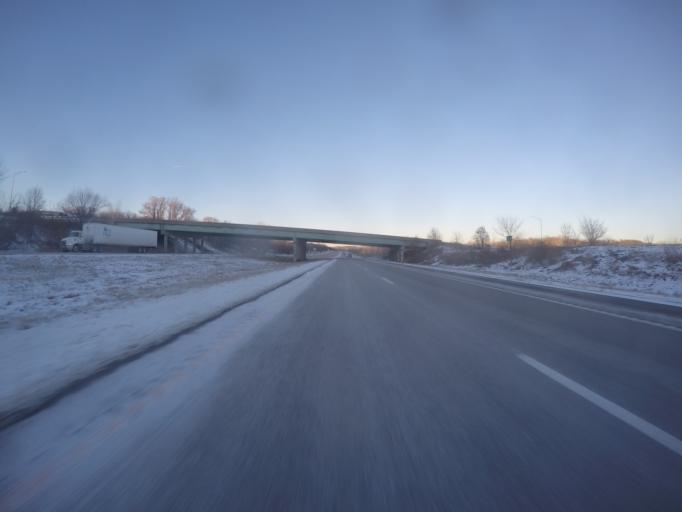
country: US
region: Missouri
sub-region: Platte County
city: Weatherby Lake
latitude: 39.2240
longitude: -94.7620
